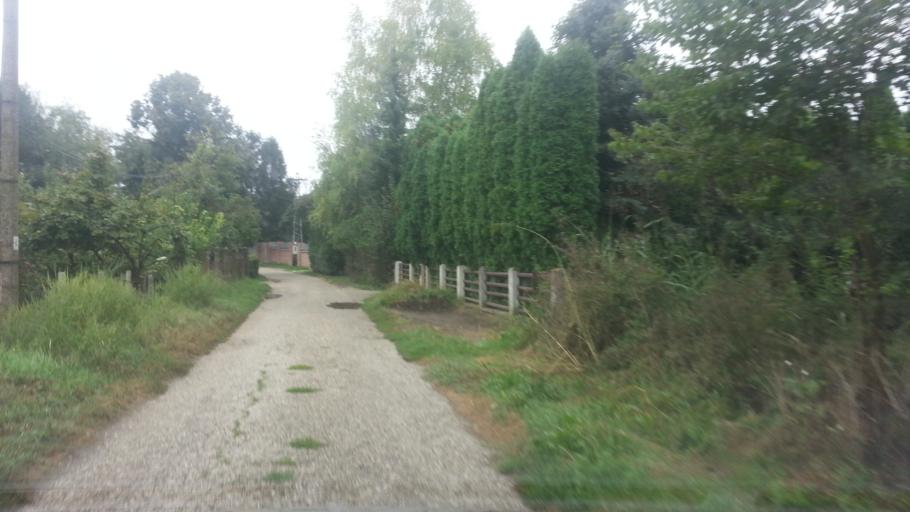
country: RS
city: Novi Banovci
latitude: 44.9430
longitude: 20.2939
